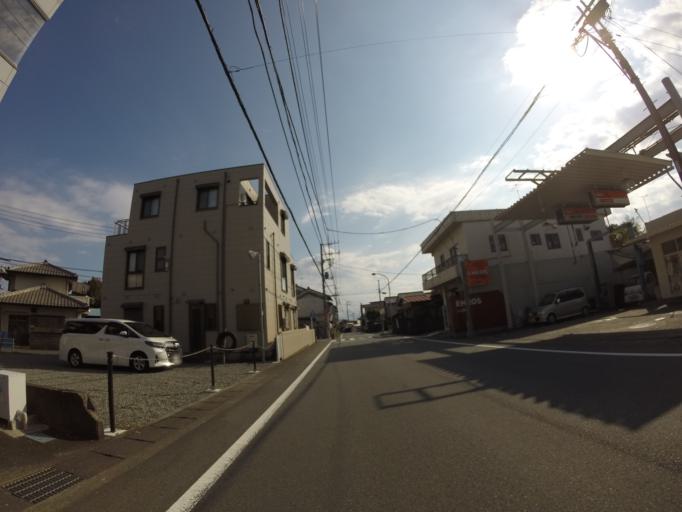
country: JP
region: Shizuoka
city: Fujinomiya
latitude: 35.1891
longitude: 138.6455
